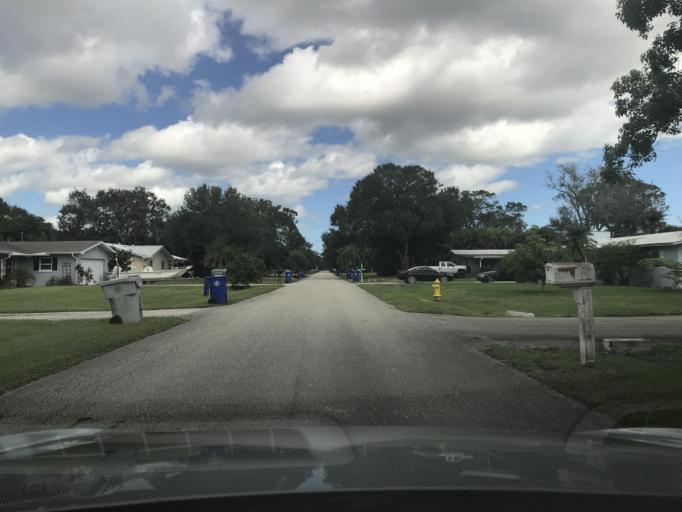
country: US
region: Florida
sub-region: Indian River County
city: Vero Beach South
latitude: 27.6430
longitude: -80.4348
